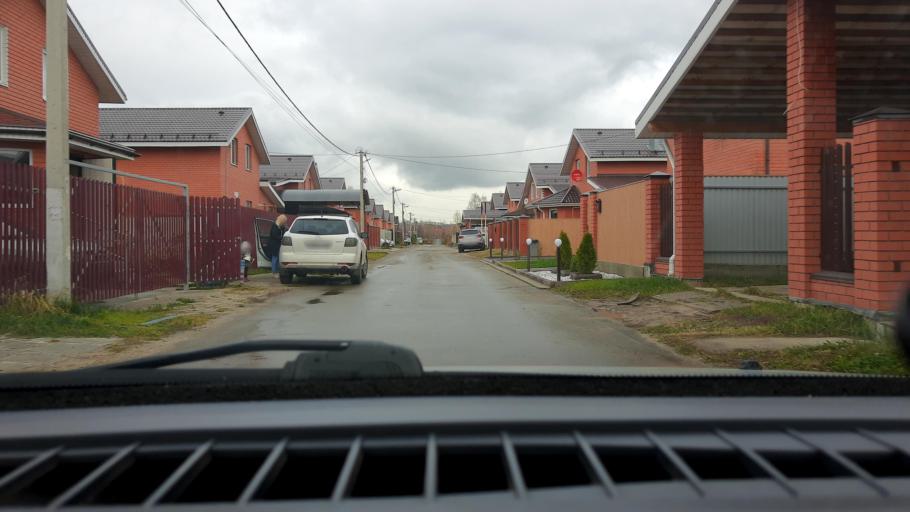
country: RU
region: Nizjnij Novgorod
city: Afonino
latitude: 56.2030
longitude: 44.1263
